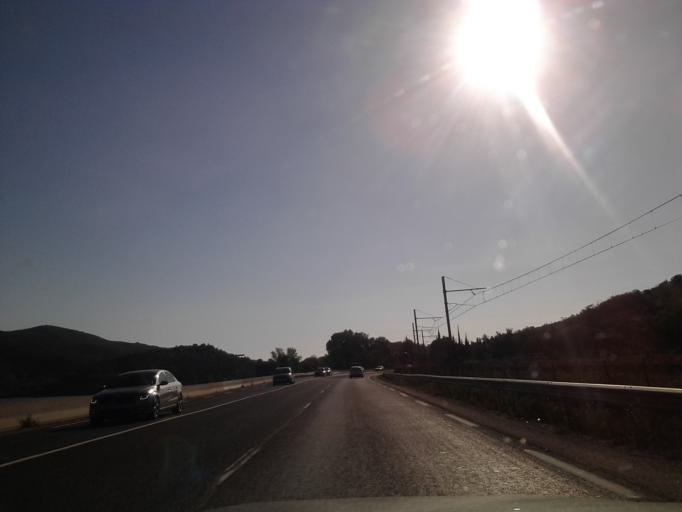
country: FR
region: Languedoc-Roussillon
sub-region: Departement des Pyrenees-Orientales
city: Vinca
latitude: 42.6506
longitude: 2.5341
